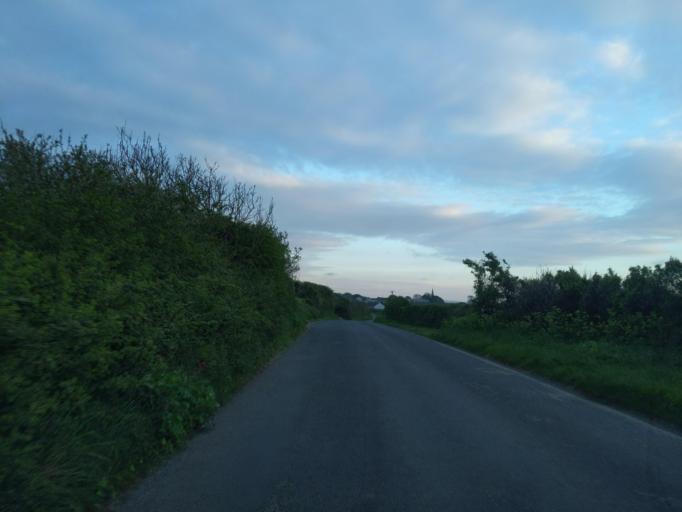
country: GB
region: England
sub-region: Cornwall
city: Polzeath
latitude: 50.5647
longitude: -4.8714
